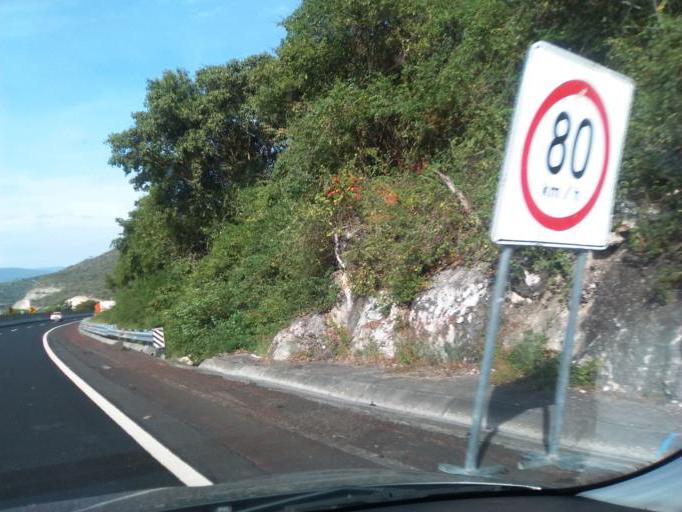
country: MX
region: Morelos
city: Tilzapotla
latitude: 18.4319
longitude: -99.1781
